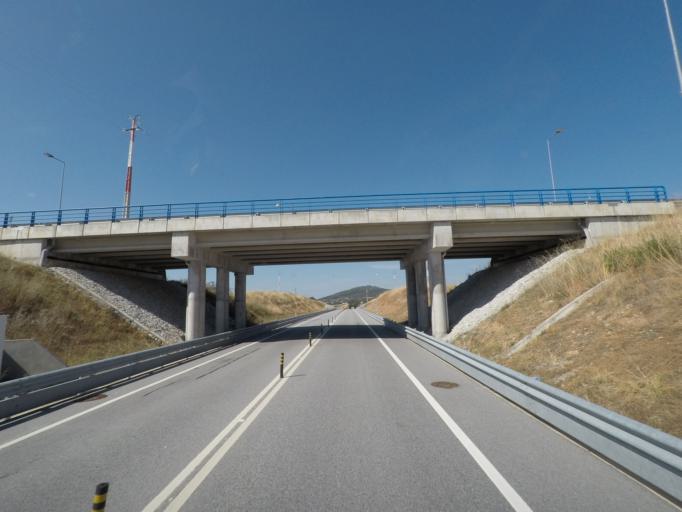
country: ES
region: Castille and Leon
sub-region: Provincia de Salamanca
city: Villarino de los Aires
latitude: 41.3569
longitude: -6.5724
